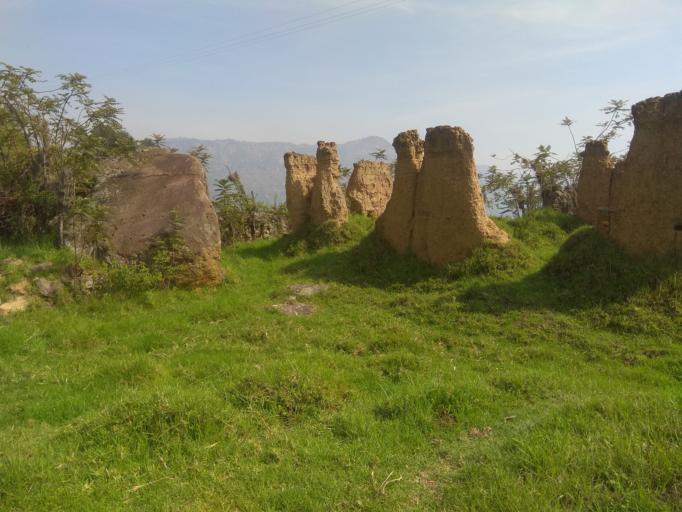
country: CO
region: Boyaca
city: Socha Viejo
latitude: 5.9817
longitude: -72.7093
